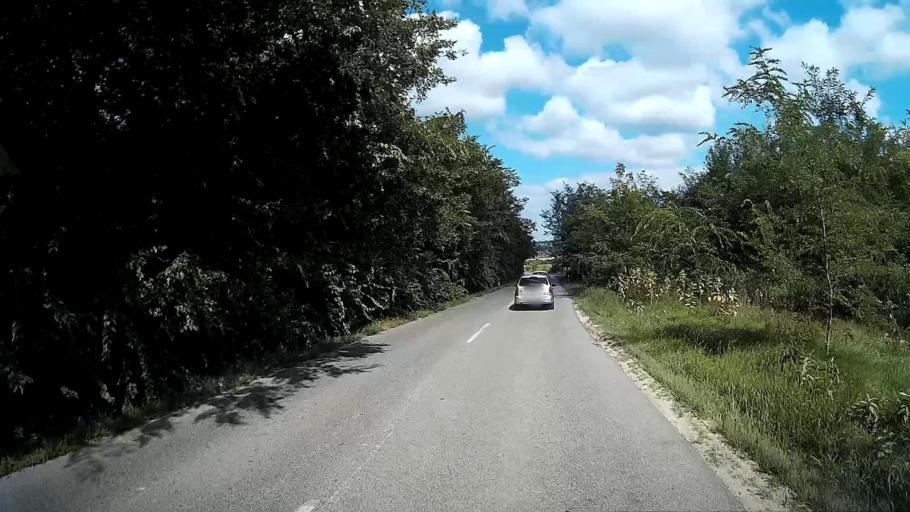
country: HU
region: Pest
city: Mogyorod
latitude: 47.5850
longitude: 19.2309
